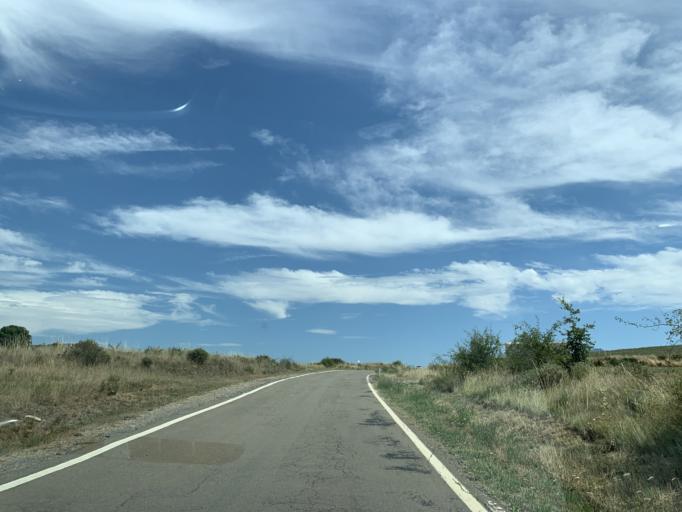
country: ES
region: Aragon
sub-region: Provincia de Huesca
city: Santa Cruz de la Seros
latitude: 42.5972
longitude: -0.6526
